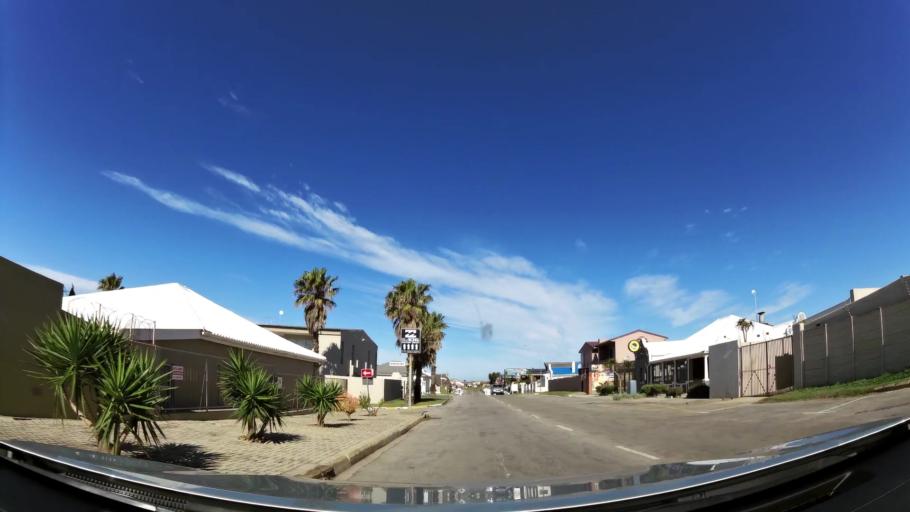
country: ZA
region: Eastern Cape
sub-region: Cacadu District Municipality
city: Jeffrey's Bay
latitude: -34.0553
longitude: 24.9226
